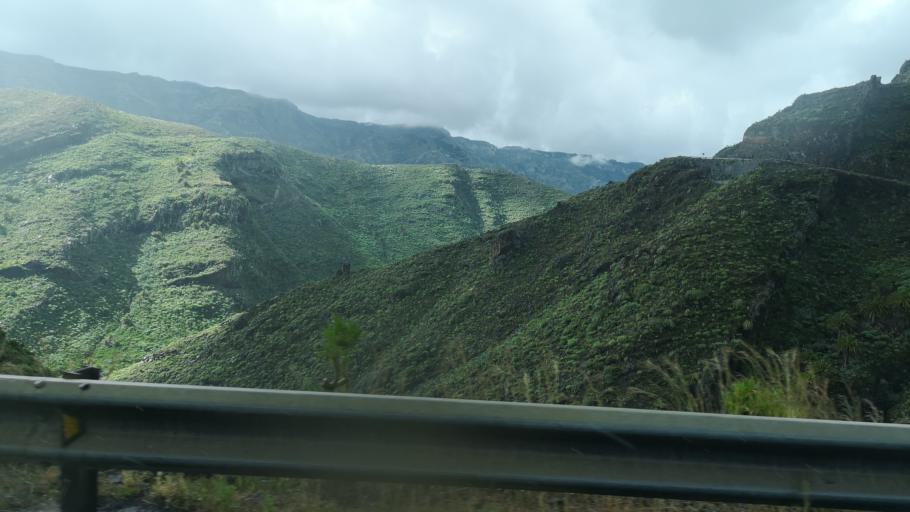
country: ES
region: Canary Islands
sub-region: Provincia de Santa Cruz de Tenerife
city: San Sebastian de la Gomera
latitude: 28.1232
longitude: -17.1456
